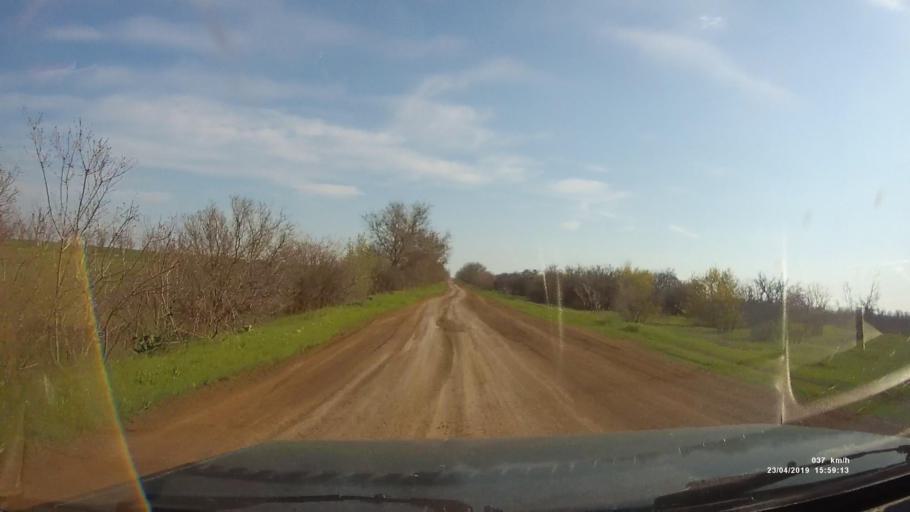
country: RU
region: Rostov
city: Remontnoye
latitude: 46.5183
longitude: 43.1096
